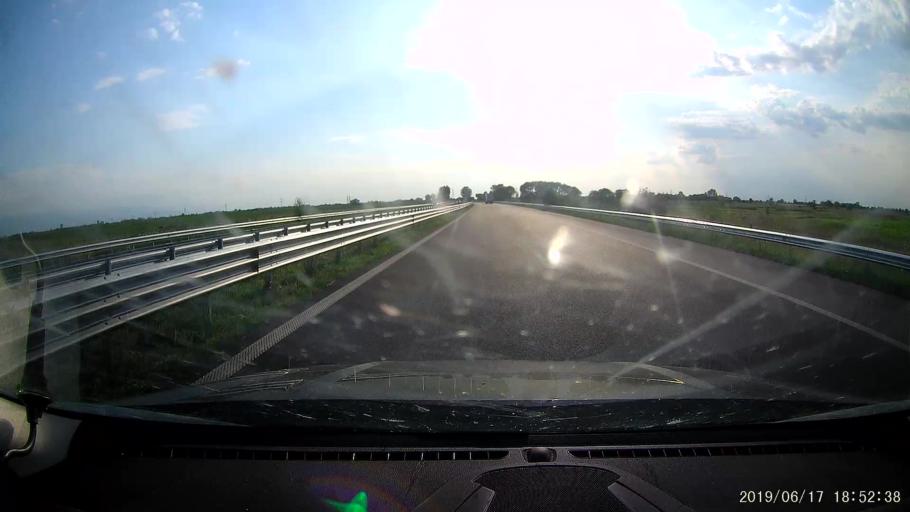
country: BG
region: Plovdiv
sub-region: Obshtina Sadovo
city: Sadovo
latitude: 42.2162
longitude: 24.9363
